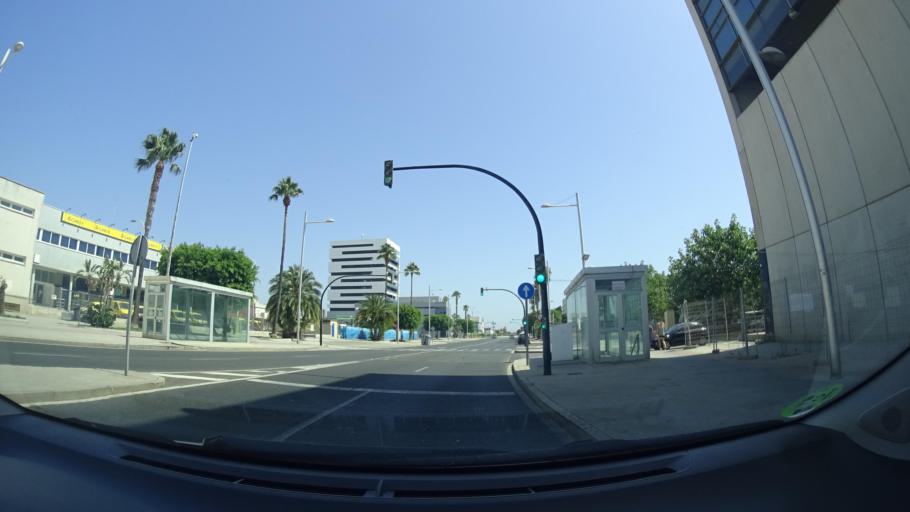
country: ES
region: Andalusia
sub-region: Provincia de Cadiz
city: Cadiz
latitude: 36.5024
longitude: -6.2719
